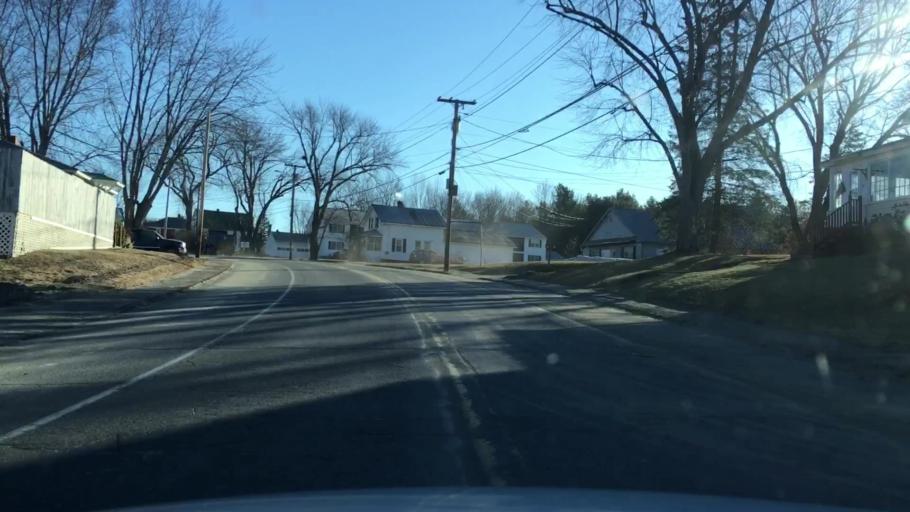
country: US
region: Maine
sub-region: Kennebec County
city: Winslow
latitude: 44.5420
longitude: -69.6201
